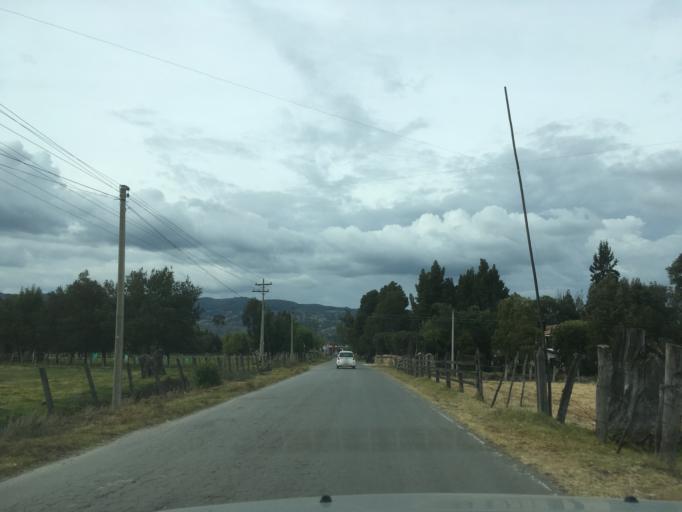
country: CO
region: Boyaca
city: Firavitoba
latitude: 5.6607
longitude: -72.9910
